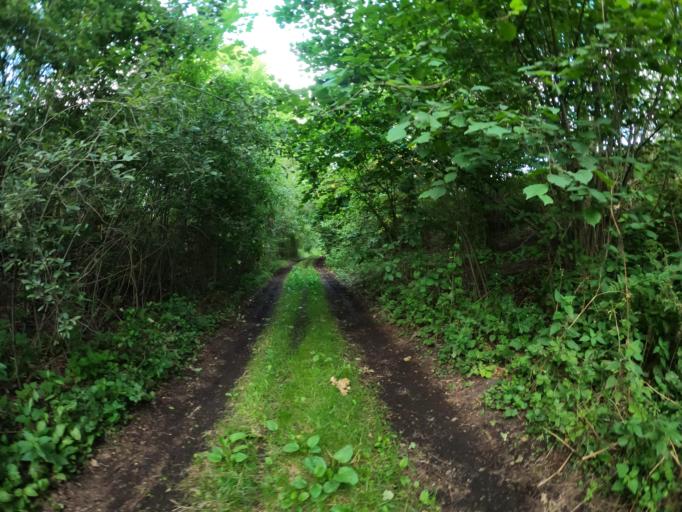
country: PL
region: West Pomeranian Voivodeship
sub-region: Powiat szczecinecki
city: Grzmiaca
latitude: 53.8645
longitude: 16.4430
